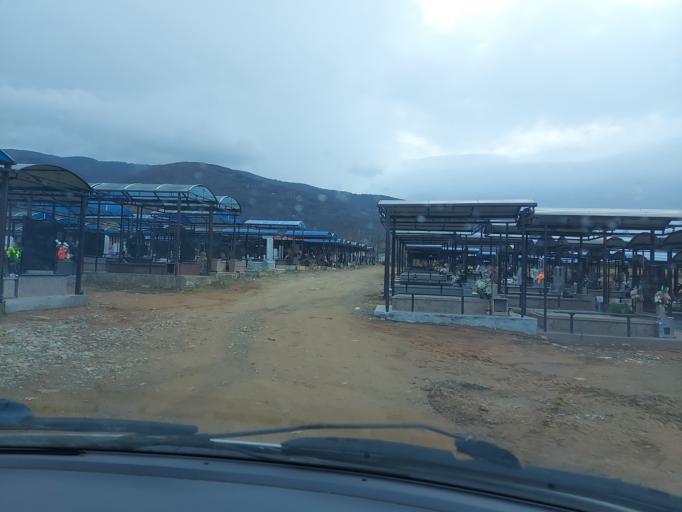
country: MK
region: Kriva Palanka
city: Kriva Palanka
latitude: 42.1869
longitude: 22.2941
